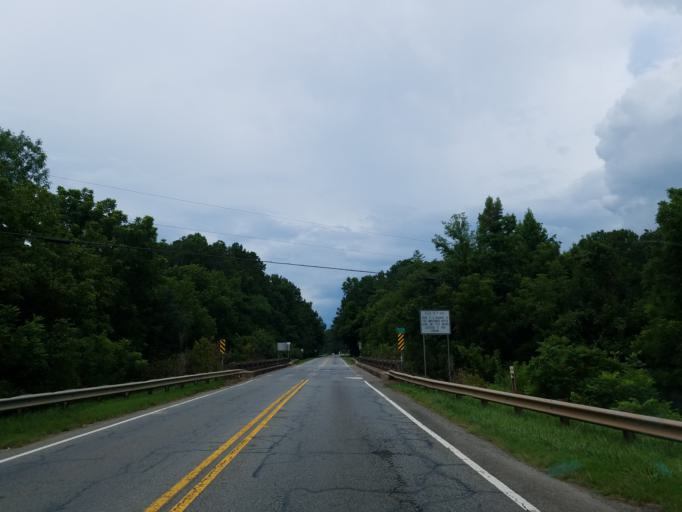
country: US
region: Georgia
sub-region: Bartow County
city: Cartersville
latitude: 34.2610
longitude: -84.8604
